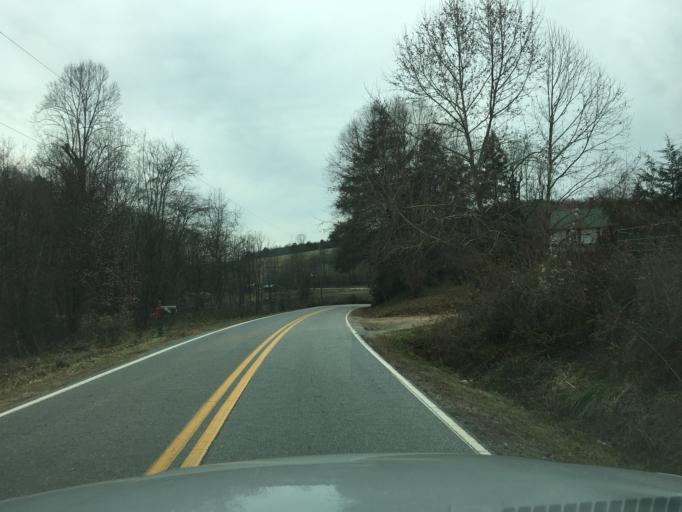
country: US
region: North Carolina
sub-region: McDowell County
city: West Marion
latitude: 35.6315
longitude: -81.9627
